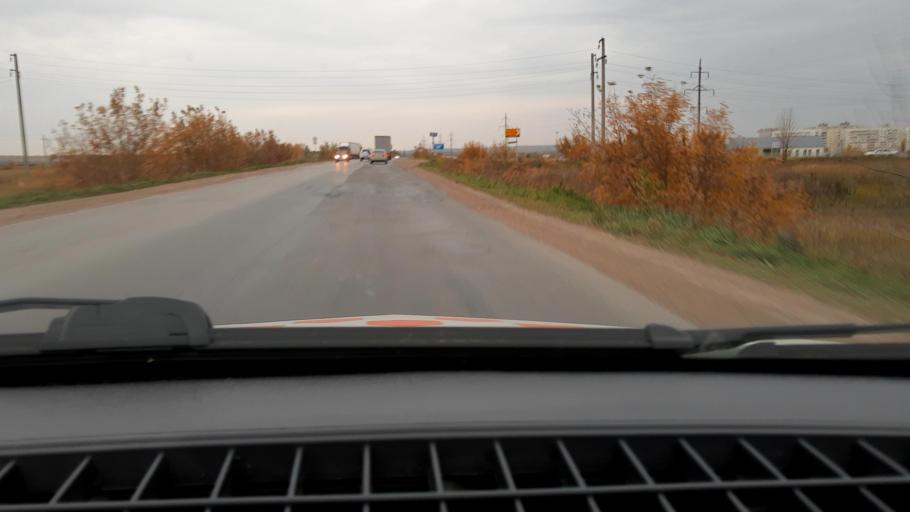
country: RU
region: Bashkortostan
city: Iglino
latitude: 54.7595
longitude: 56.2598
